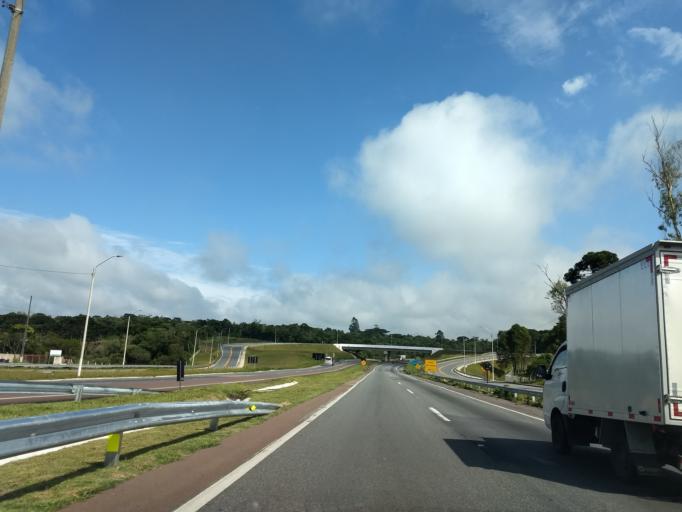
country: BR
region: Parana
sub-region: Sao Jose Dos Pinhais
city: Sao Jose dos Pinhais
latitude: -25.8226
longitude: -49.1279
